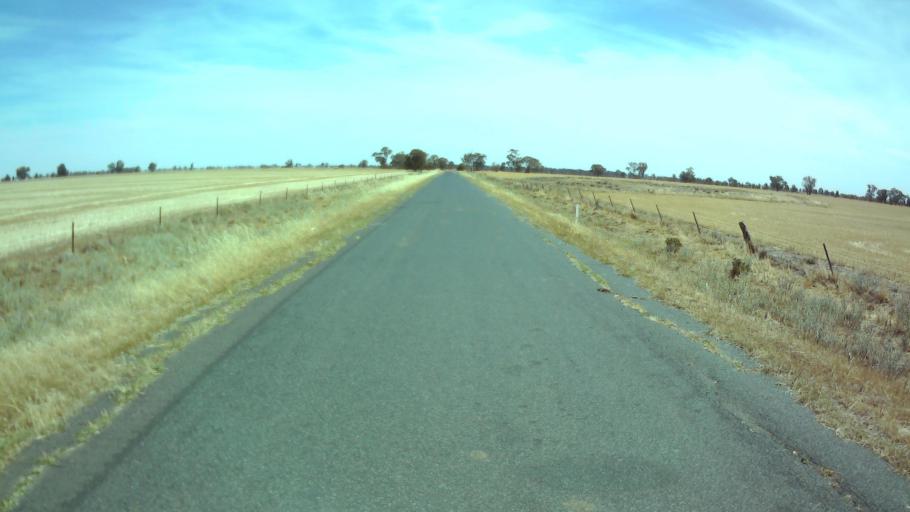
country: AU
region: New South Wales
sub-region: Weddin
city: Grenfell
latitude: -33.9323
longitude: 147.7620
